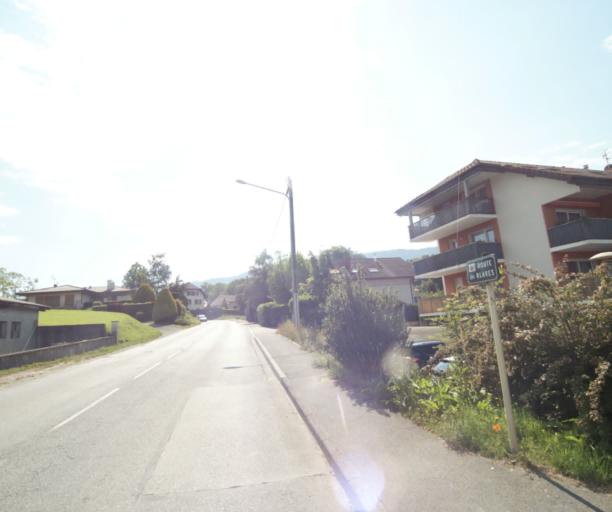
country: FR
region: Rhone-Alpes
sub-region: Departement de la Haute-Savoie
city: Allinges
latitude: 46.3350
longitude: 6.4793
